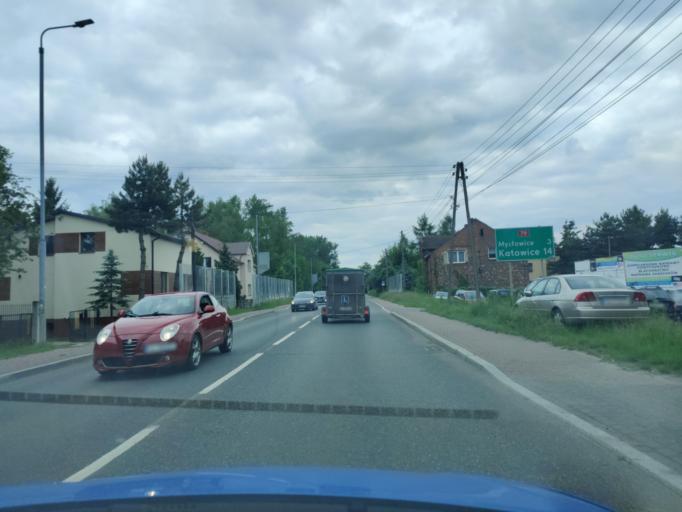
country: PL
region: Silesian Voivodeship
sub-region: Myslowice
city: Myslowice
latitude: 50.2314
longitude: 19.1629
